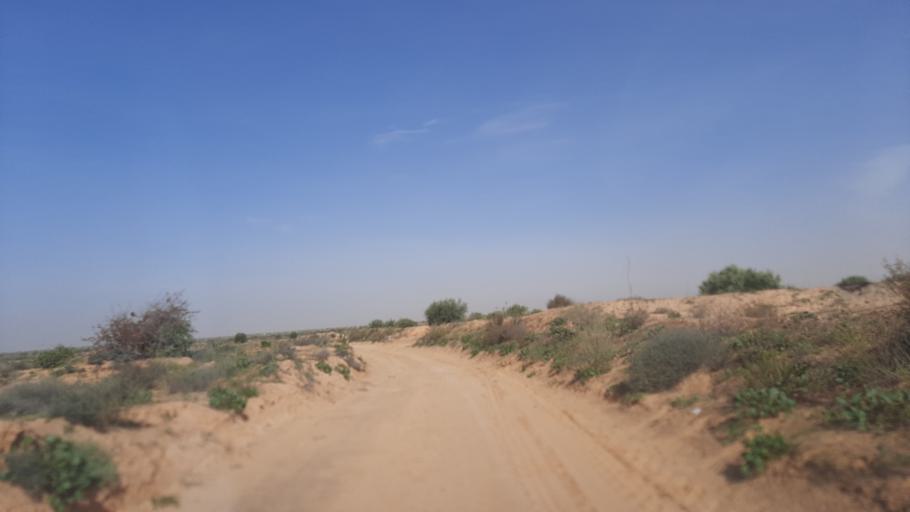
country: TN
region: Madanin
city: Zarzis
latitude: 33.4421
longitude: 10.8082
